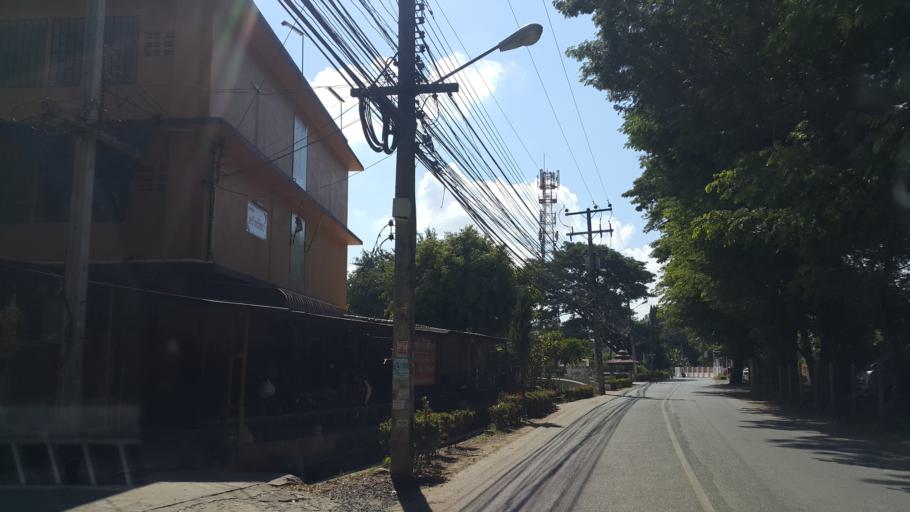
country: TH
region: Chiang Mai
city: San Sai
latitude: 18.8298
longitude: 99.0202
